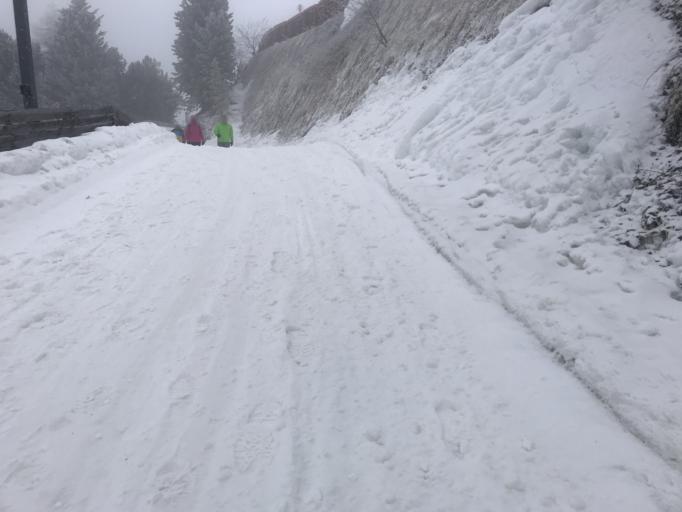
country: IT
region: Trentino-Alto Adige
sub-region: Bolzano
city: San Pietro
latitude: 46.6845
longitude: 11.7100
